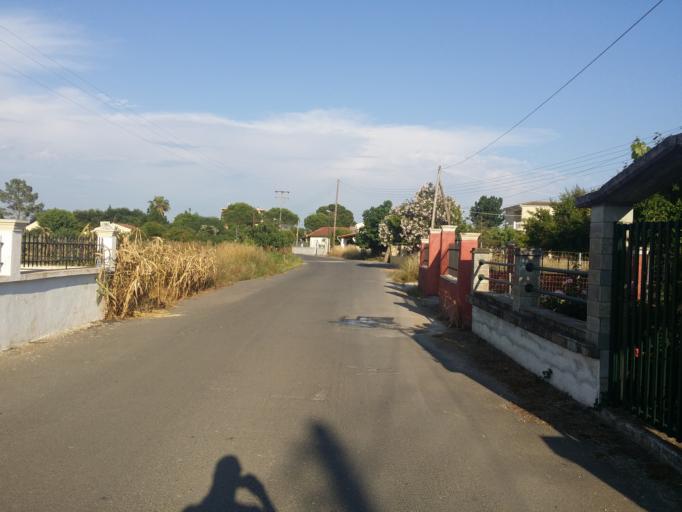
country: GR
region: Ionian Islands
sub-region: Nomos Kerkyras
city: Perivoli
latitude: 39.4287
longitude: 19.9460
